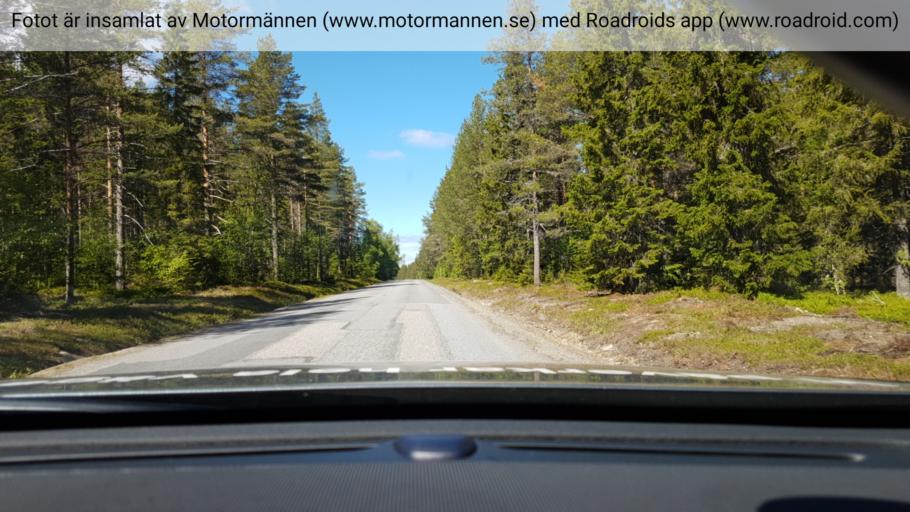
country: SE
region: Vaesterbotten
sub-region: Skelleftea Kommun
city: Burea
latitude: 64.4489
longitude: 21.4623
